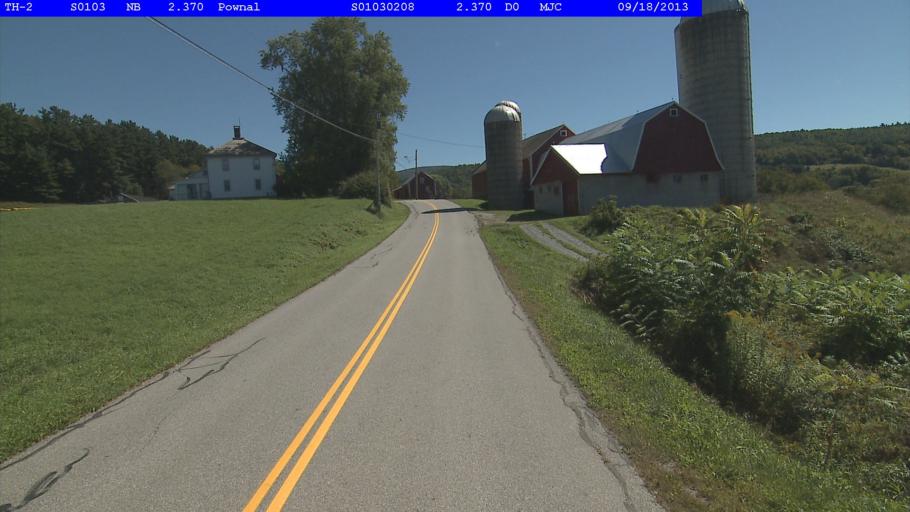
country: US
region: Vermont
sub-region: Bennington County
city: Bennington
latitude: 42.7978
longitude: -73.2317
